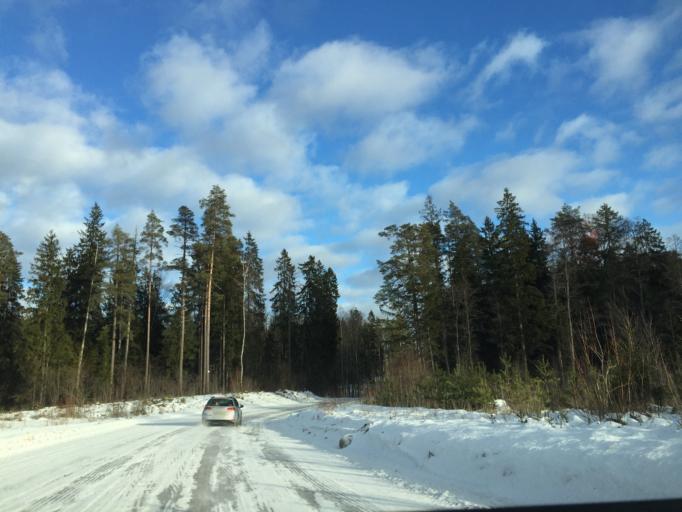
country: LV
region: Ogre
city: Jumprava
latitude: 56.5929
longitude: 24.9820
